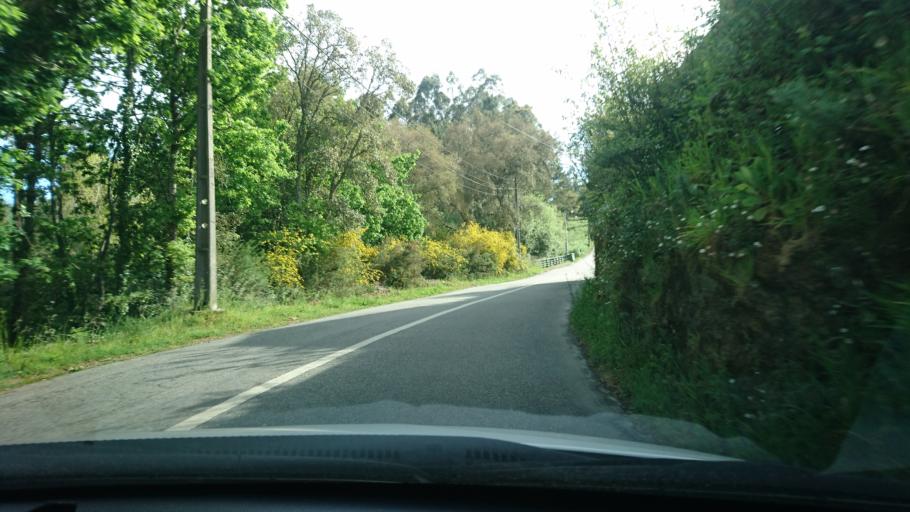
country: PT
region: Aveiro
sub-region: Oliveira de Azemeis
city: Sao Roque
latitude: 40.8789
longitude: -8.4840
